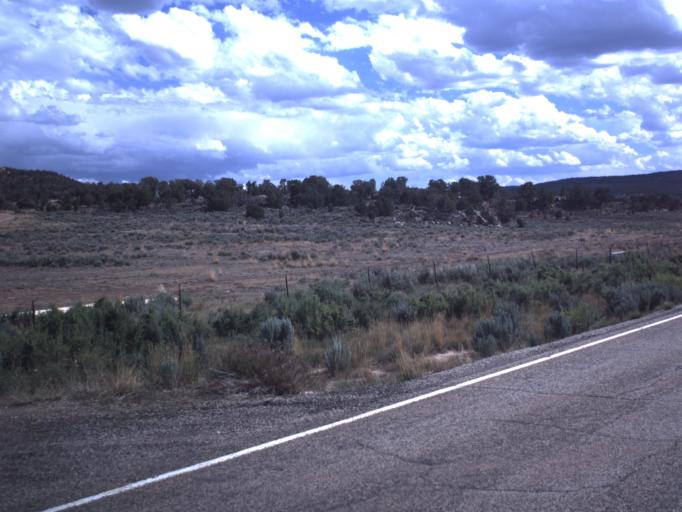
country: US
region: Utah
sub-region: Duchesne County
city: Duchesne
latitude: 40.2334
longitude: -110.7183
